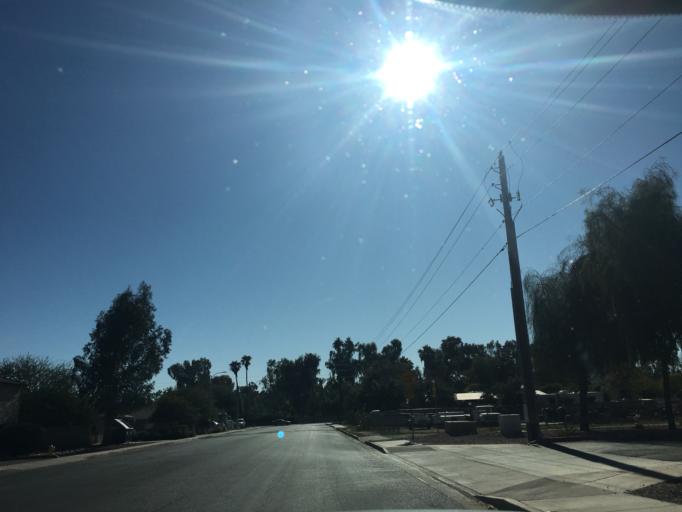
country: US
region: Arizona
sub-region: Maricopa County
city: Mesa
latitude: 33.4456
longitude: -111.8440
